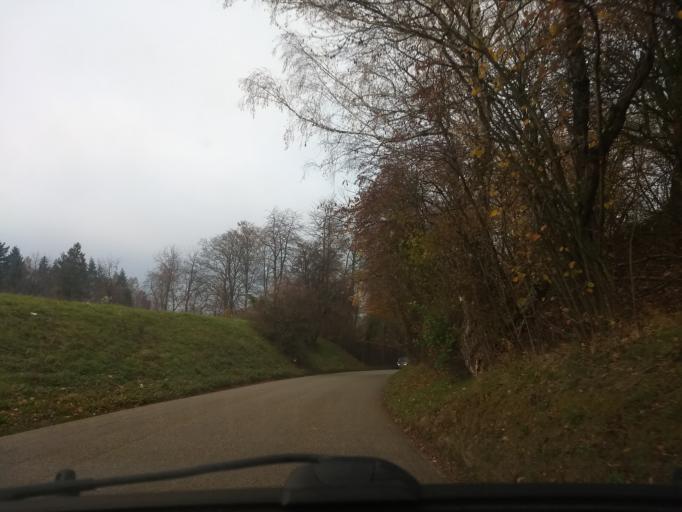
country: DE
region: Baden-Wuerttemberg
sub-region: Karlsruhe Region
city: Baden-Baden
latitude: 48.7897
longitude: 8.2135
